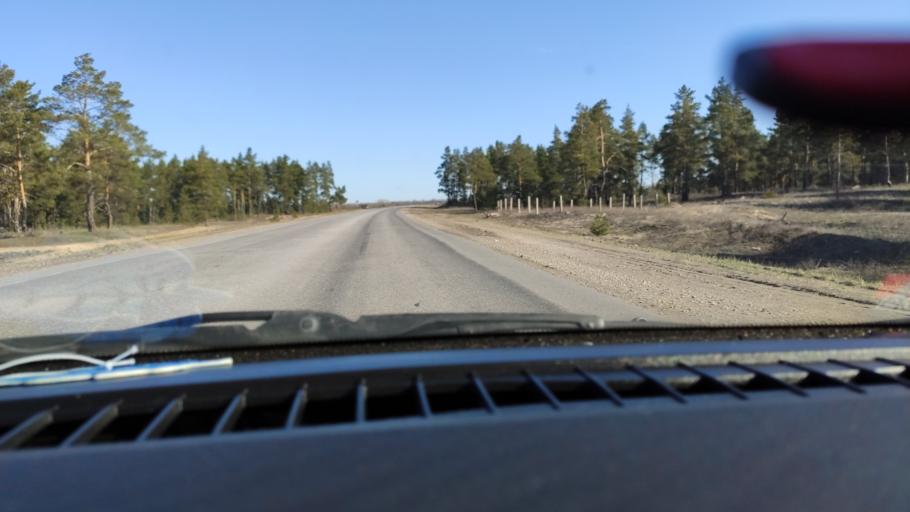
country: RU
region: Samara
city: Varlamovo
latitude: 53.1479
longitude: 48.2843
